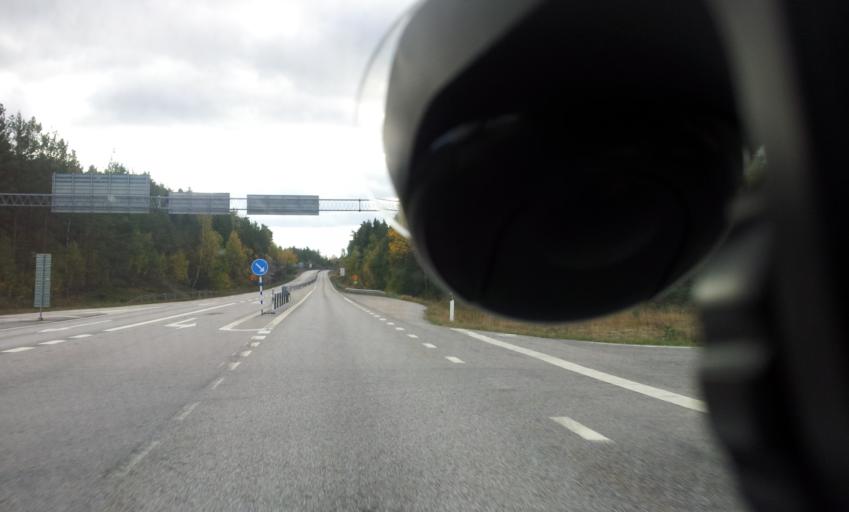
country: SE
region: OEstergoetland
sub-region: Valdemarsviks Kommun
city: Valdemarsvik
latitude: 58.1602
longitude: 16.5428
